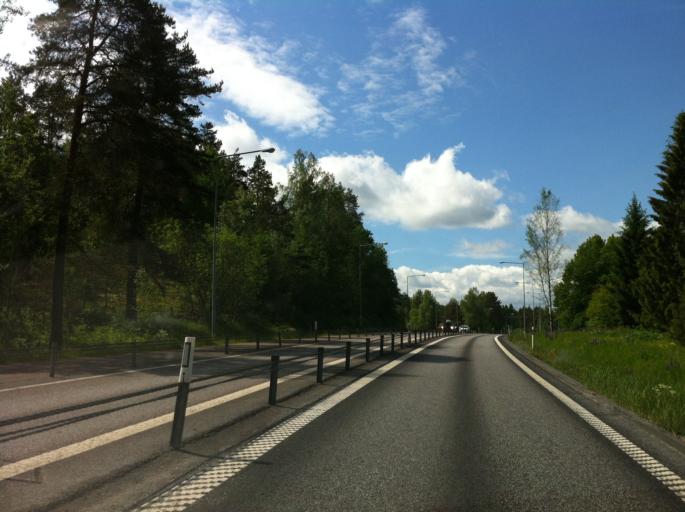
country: SE
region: Vaermland
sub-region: Grums Kommun
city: Slottsbron
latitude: 59.3182
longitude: 13.1035
